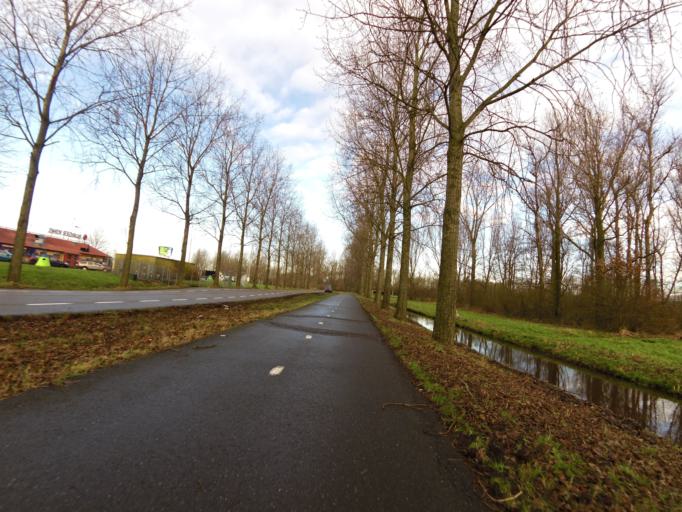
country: NL
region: South Holland
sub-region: Gemeente Delft
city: Delft
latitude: 51.9844
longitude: 4.3964
